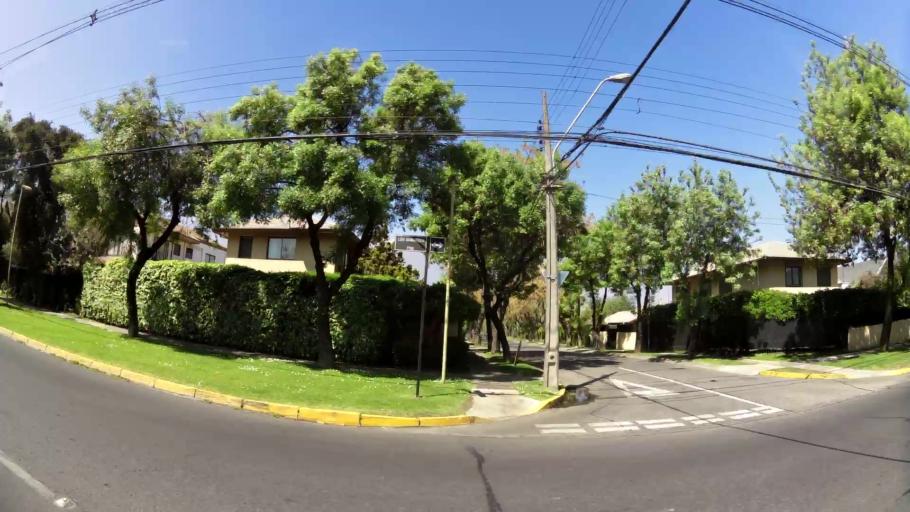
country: CL
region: Santiago Metropolitan
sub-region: Provincia de Santiago
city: Villa Presidente Frei, Nunoa, Santiago, Chile
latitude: -33.4132
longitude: -70.5479
